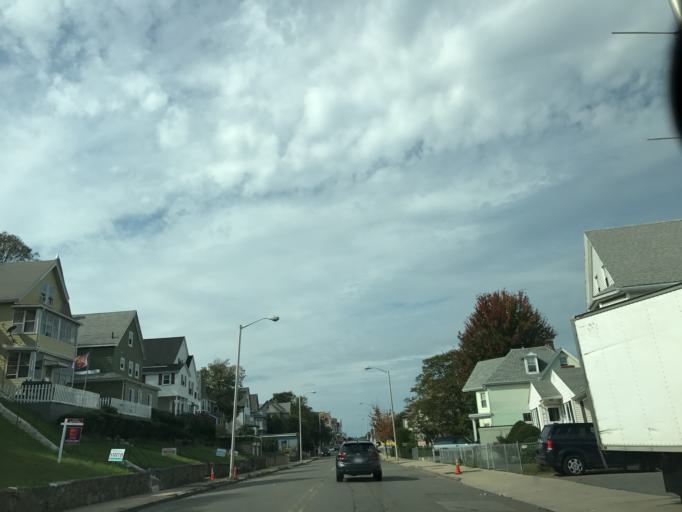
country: US
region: Massachusetts
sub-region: Middlesex County
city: Everett
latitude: 42.4185
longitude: -71.0515
